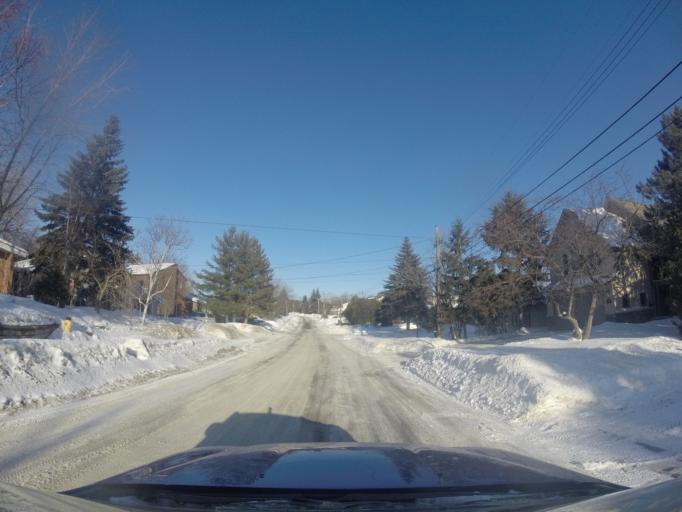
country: CA
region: Ontario
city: Greater Sudbury
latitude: 46.4624
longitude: -80.9922
